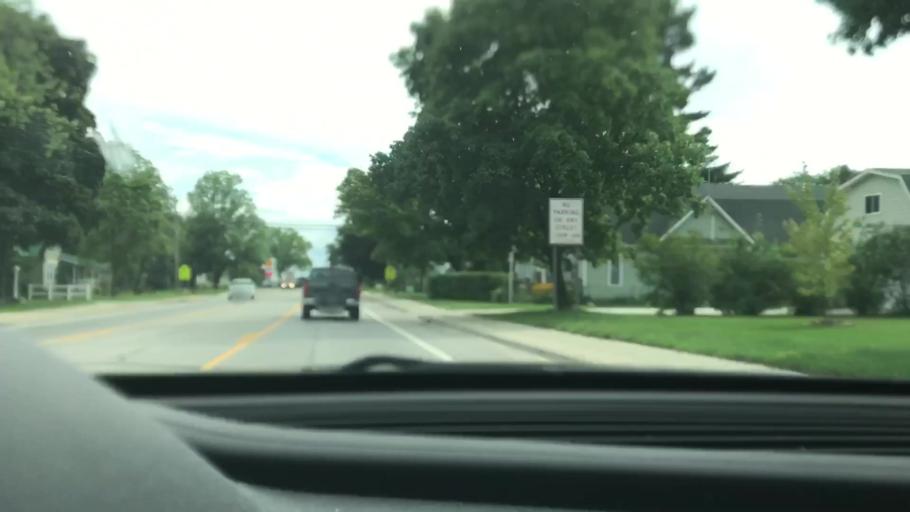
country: US
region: Michigan
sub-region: Missaukee County
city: Lake City
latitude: 44.3377
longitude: -85.2148
